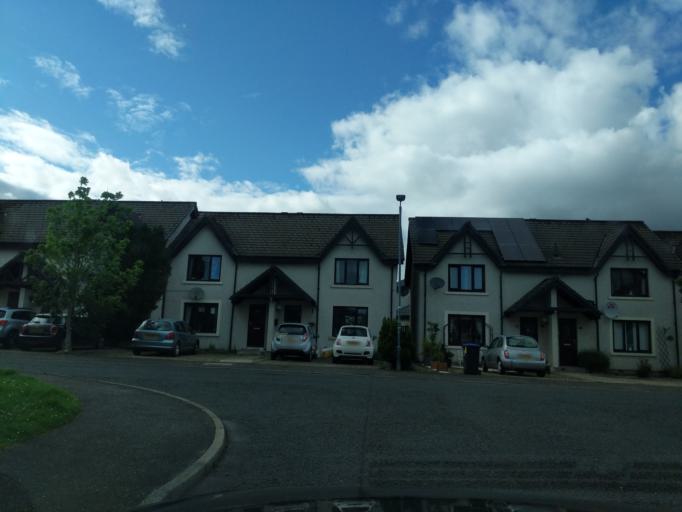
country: GB
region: Scotland
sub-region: The Scottish Borders
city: West Linton
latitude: 55.7517
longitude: -3.3518
